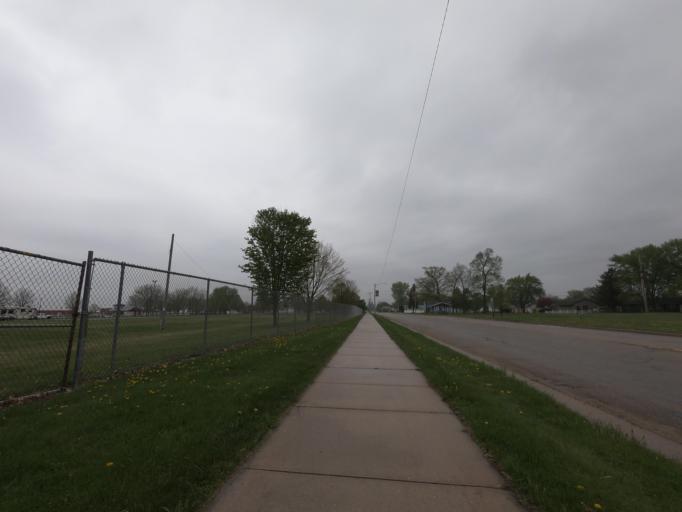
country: US
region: Wisconsin
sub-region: Jefferson County
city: Jefferson
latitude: 43.0108
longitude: -88.8173
